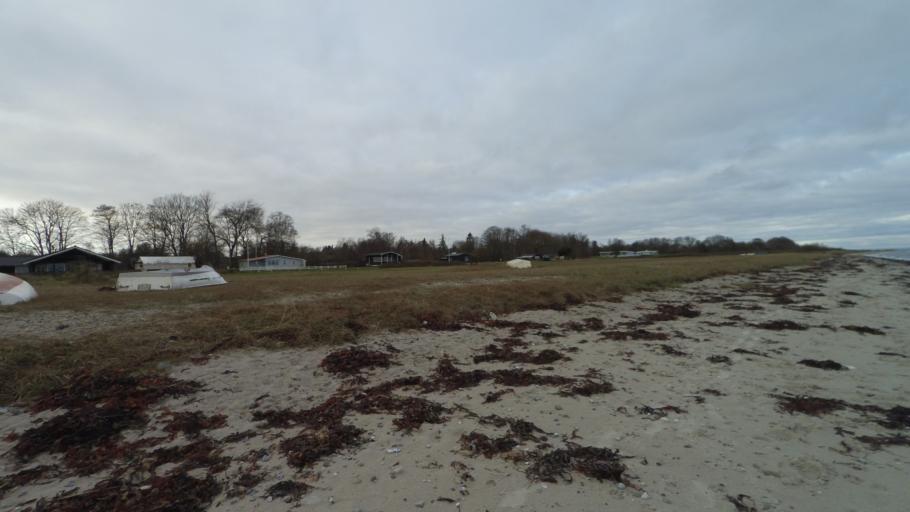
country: DK
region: Central Jutland
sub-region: Arhus Kommune
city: Beder
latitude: 56.0418
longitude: 10.2711
